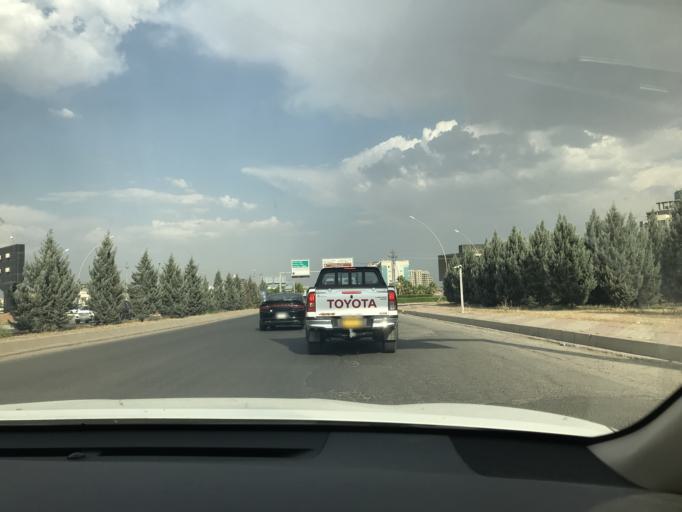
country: IQ
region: Arbil
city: Erbil
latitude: 36.2048
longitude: 43.9657
